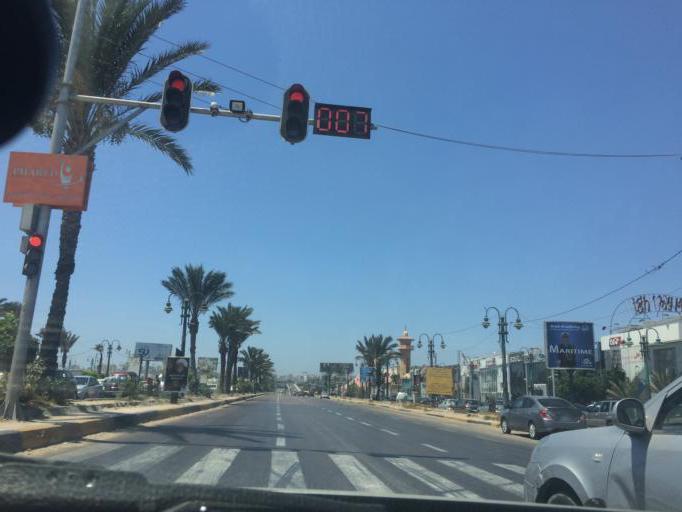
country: EG
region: Alexandria
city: Alexandria
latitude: 31.1740
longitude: 29.9322
